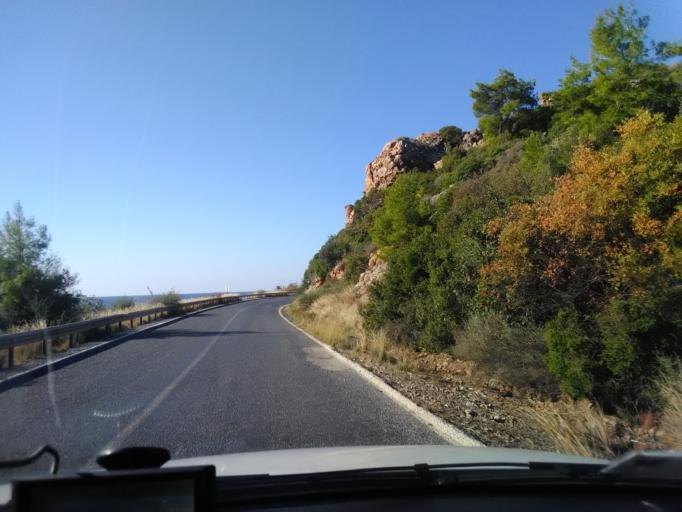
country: TR
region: Antalya
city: Gazipasa
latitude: 36.3190
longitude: 32.2401
